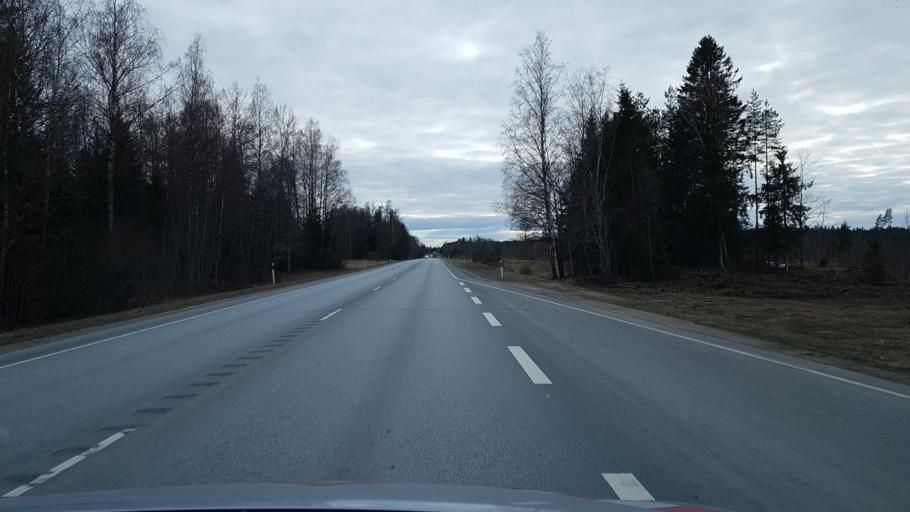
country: EE
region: Laeaene-Virumaa
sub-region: Viru-Nigula vald
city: Kunda
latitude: 59.3794
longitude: 26.5994
